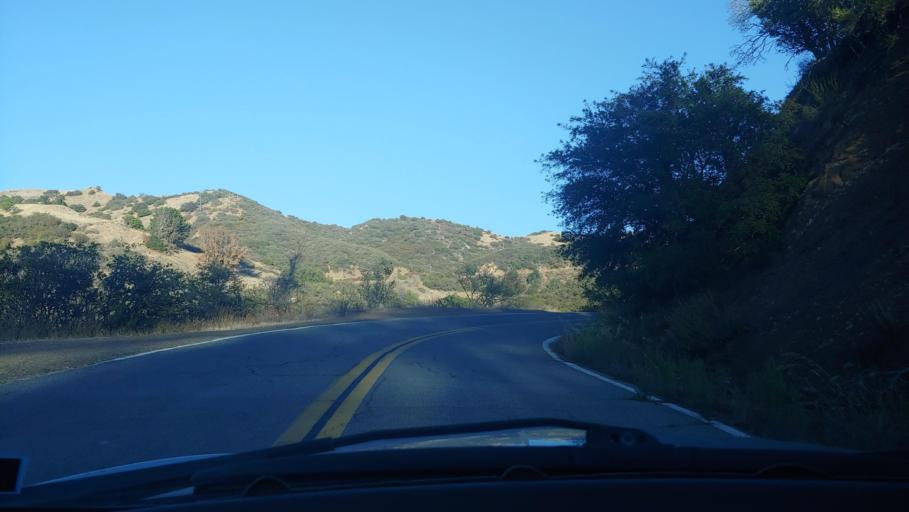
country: US
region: California
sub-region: Santa Barbara County
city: Goleta
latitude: 34.5145
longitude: -119.7991
